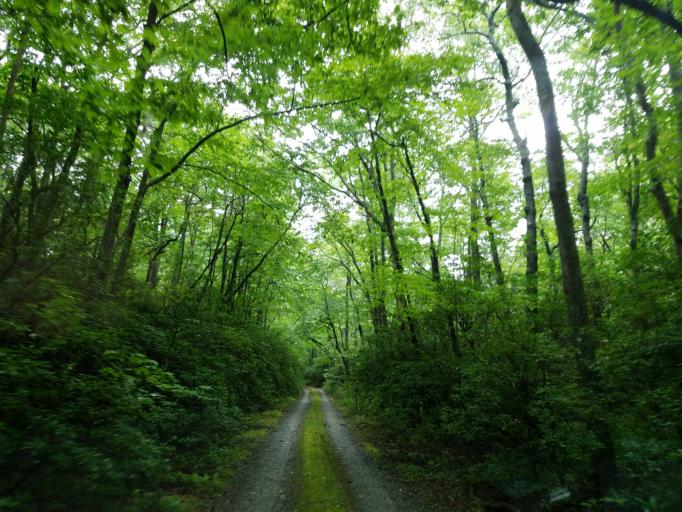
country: US
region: Georgia
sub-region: Lumpkin County
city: Dahlonega
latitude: 34.6363
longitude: -84.1609
